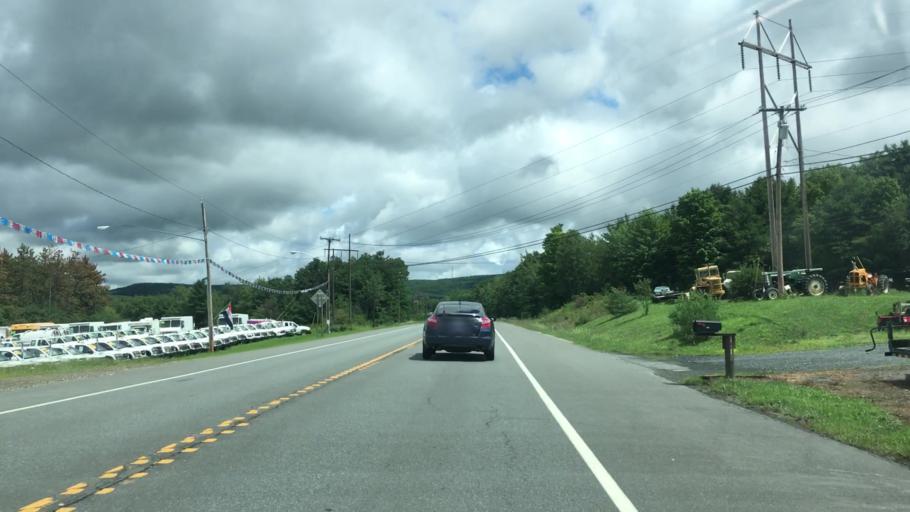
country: US
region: New York
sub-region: Rensselaer County
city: Hoosick Falls
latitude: 42.8483
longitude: -73.4412
